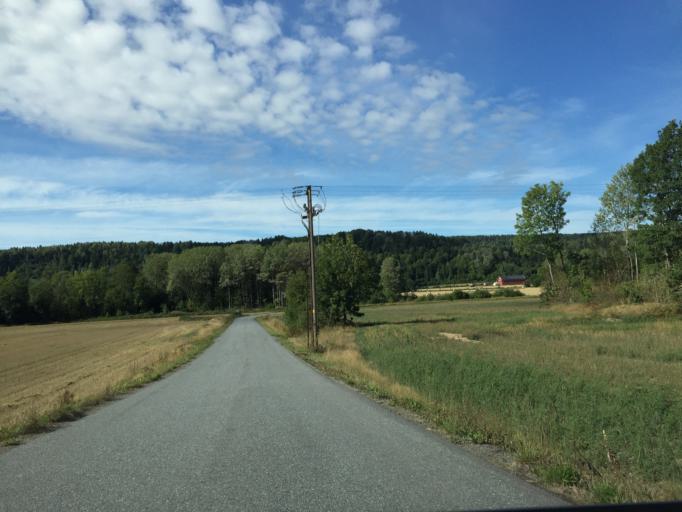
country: NO
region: Vestfold
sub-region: Holmestrand
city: Gullhaug
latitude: 59.4848
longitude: 10.1699
